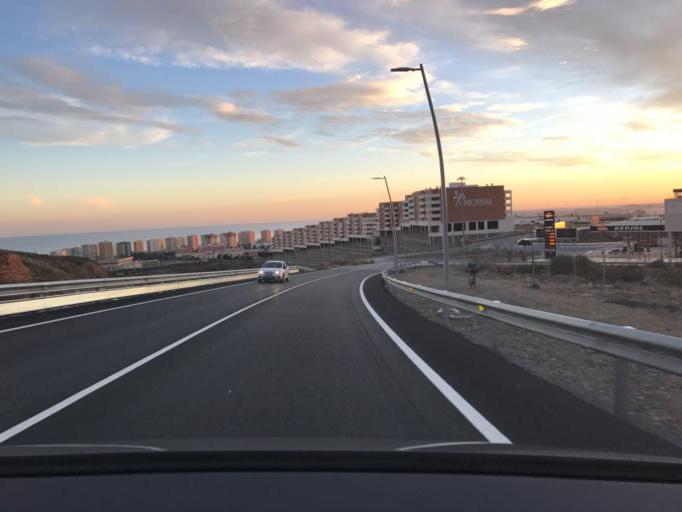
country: ES
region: Andalusia
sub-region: Provincia de Almeria
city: Aguadulce
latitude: 36.8238
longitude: -2.5818
